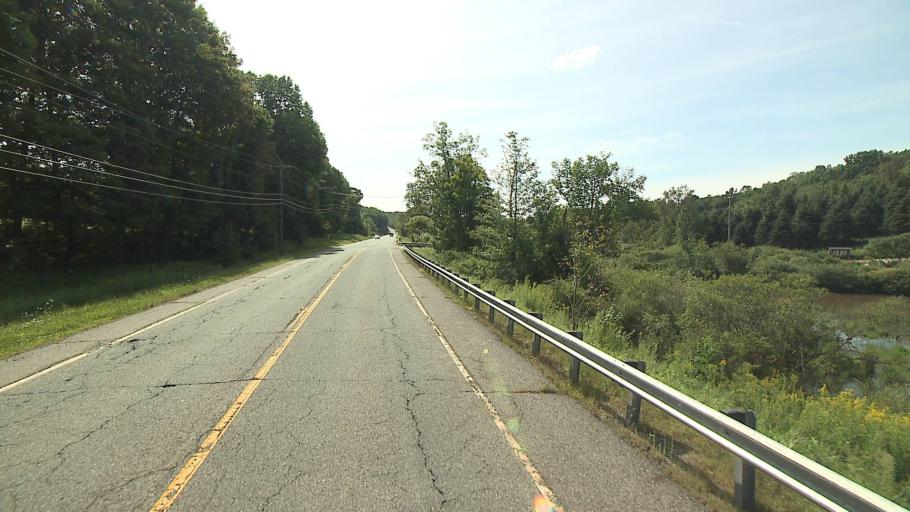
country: US
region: Connecticut
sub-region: Litchfield County
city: Litchfield
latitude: 41.7365
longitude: -73.1618
